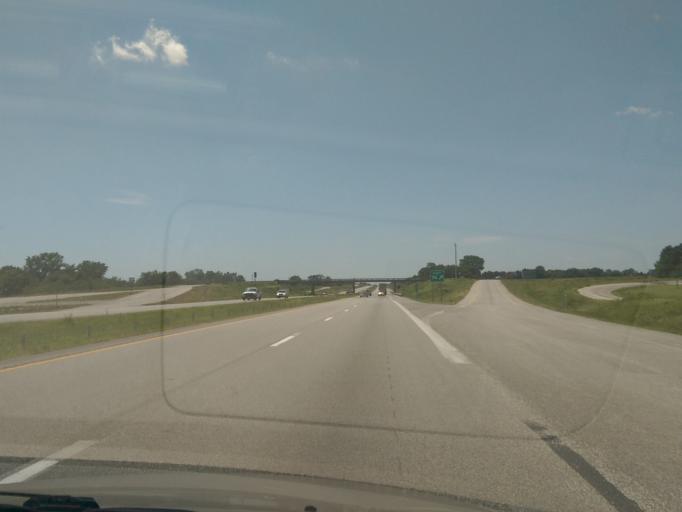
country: US
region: Missouri
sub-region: Saline County
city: Sweet Springs
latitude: 38.9715
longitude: -93.2688
